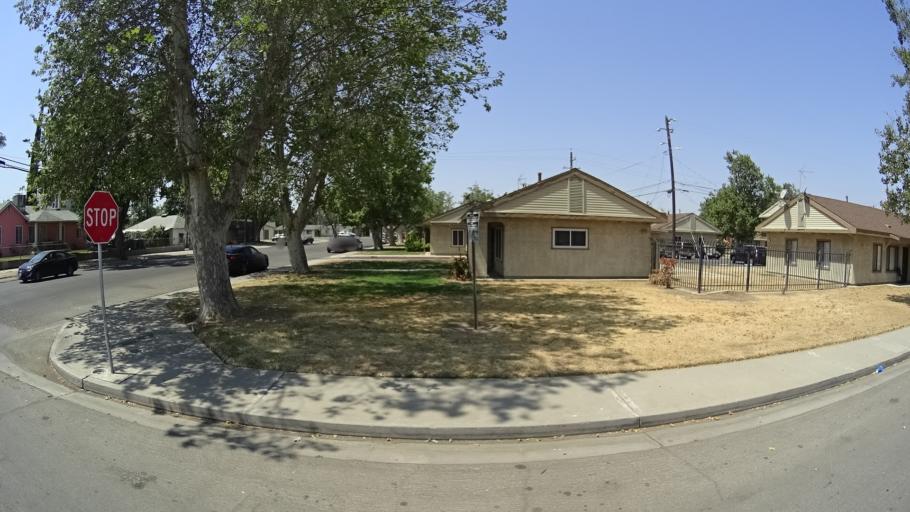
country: US
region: California
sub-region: Fresno County
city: Fresno
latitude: 36.7253
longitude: -119.8002
